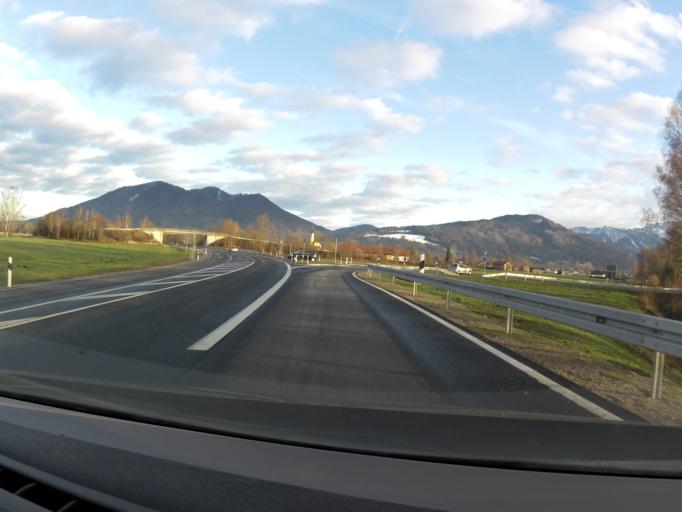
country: DE
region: Bavaria
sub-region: Upper Bavaria
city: Bichl
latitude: 47.7216
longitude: 11.3990
